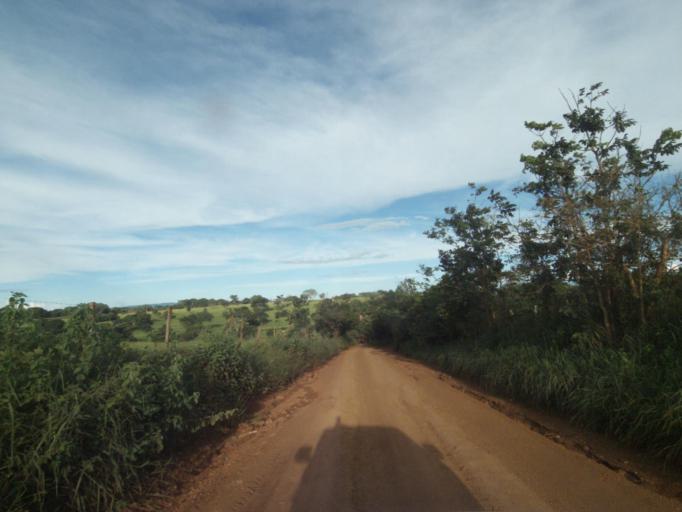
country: BR
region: Goias
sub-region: Jaragua
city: Jaragua
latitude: -15.8888
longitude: -49.4679
